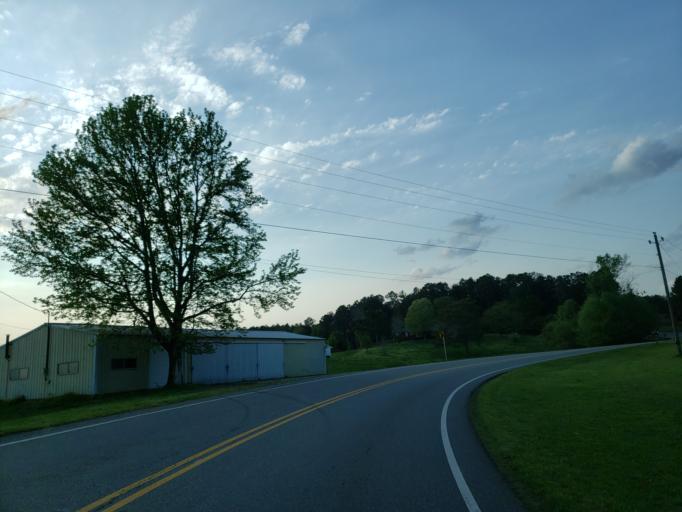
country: US
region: Georgia
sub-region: Cherokee County
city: Ball Ground
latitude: 34.2675
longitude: -84.3658
